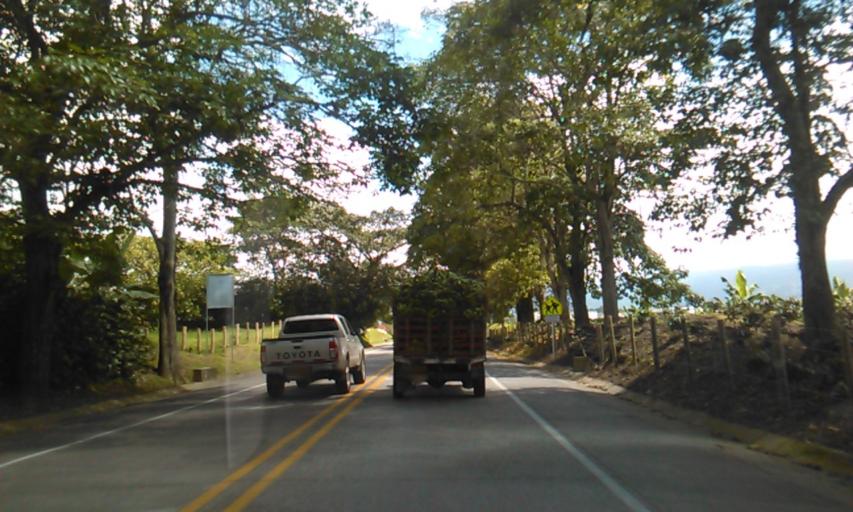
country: CO
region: Quindio
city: Armenia
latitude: 4.4925
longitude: -75.7009
